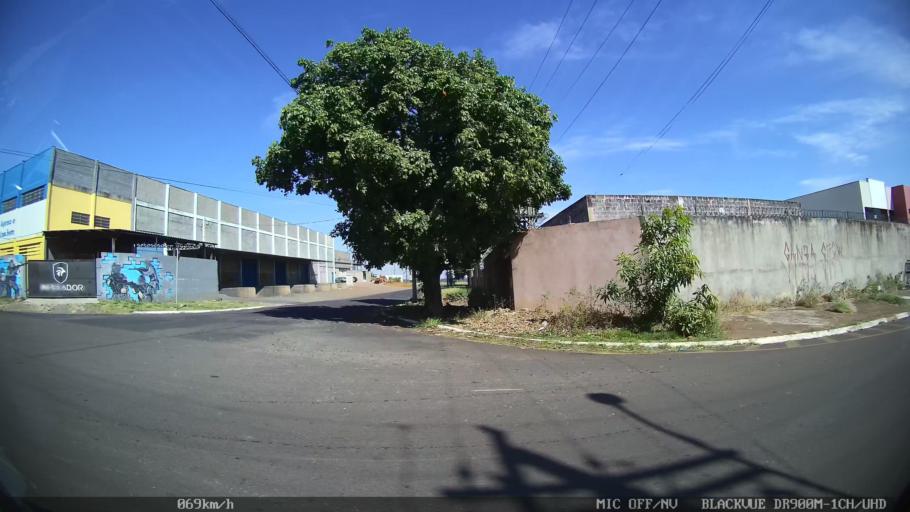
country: BR
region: Sao Paulo
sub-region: Franca
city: Franca
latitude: -20.5471
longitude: -47.4556
